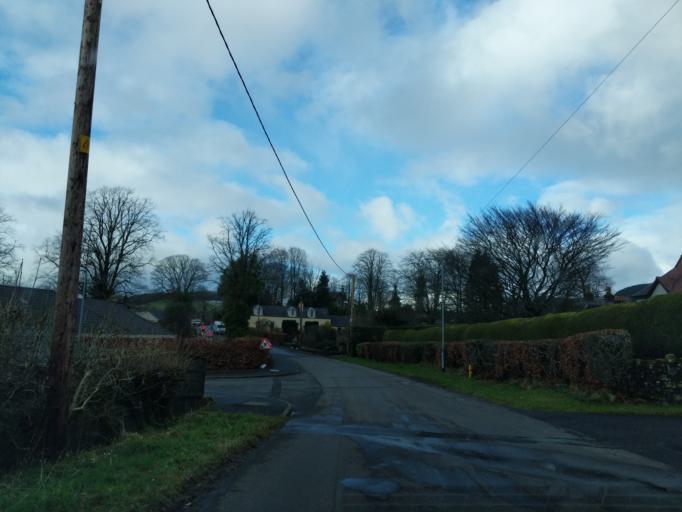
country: GB
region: Scotland
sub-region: Dumfries and Galloway
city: Moffat
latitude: 55.3264
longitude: -3.4308
